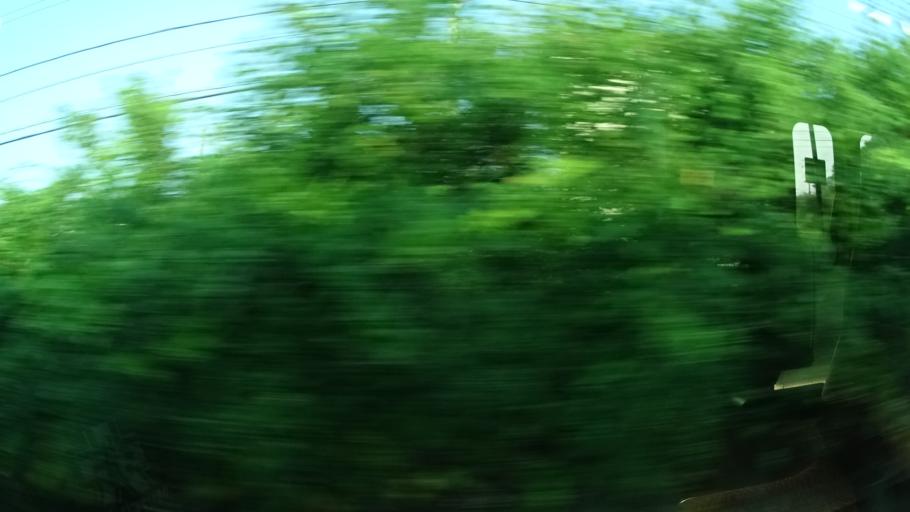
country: JP
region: Ibaraki
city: Hitachi
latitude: 36.6063
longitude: 140.6677
